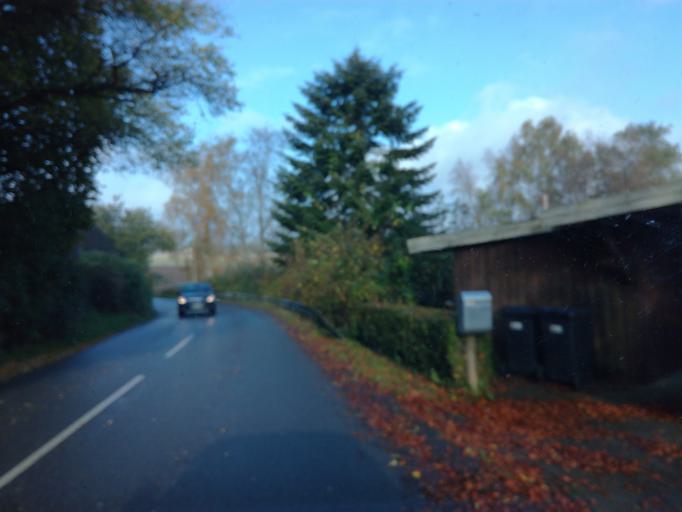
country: DK
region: South Denmark
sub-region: Vejle Kommune
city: Borkop
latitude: 55.6531
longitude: 9.6472
